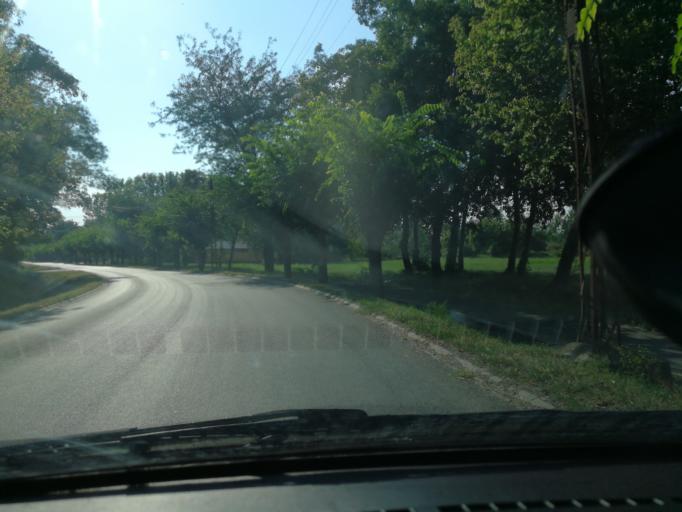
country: HU
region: Bacs-Kiskun
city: Kalocsa
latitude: 46.5349
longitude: 18.9916
